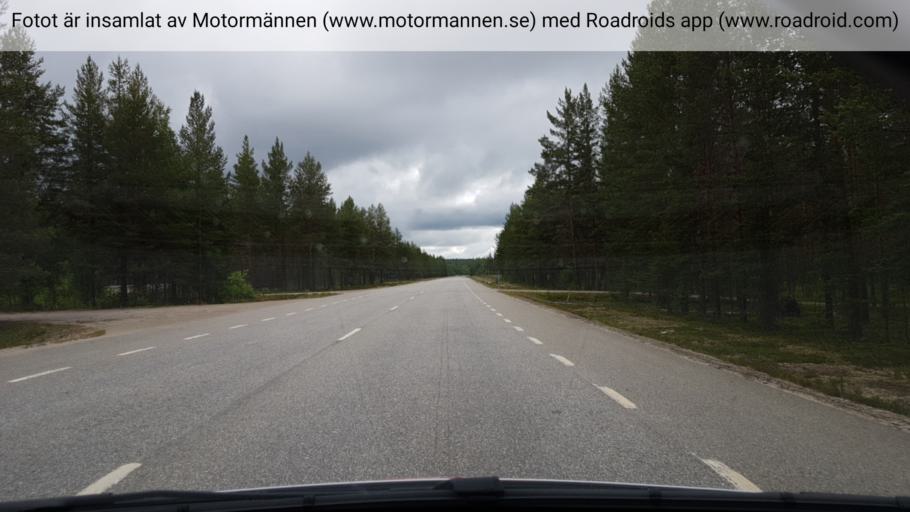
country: SE
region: Vaesterbotten
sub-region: Norsjo Kommun
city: Norsjoe
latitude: 64.6036
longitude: 19.2979
